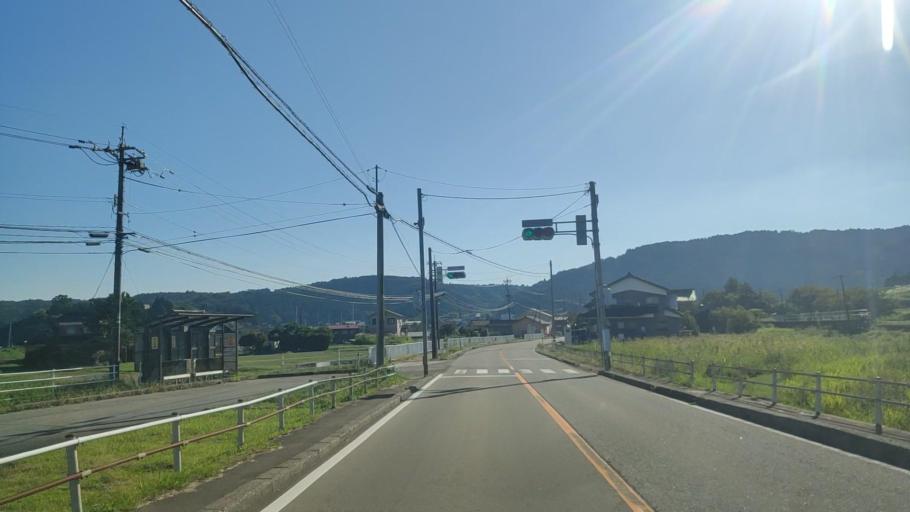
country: JP
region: Ishikawa
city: Nanao
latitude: 37.1487
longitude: 136.8762
